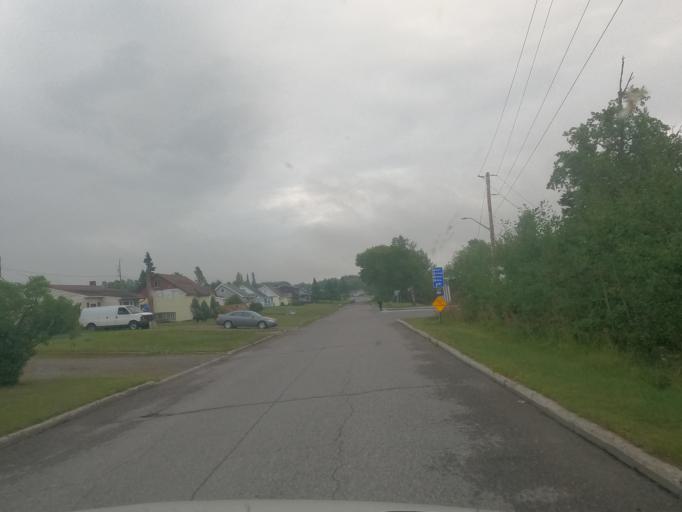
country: CA
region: Ontario
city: Marathon
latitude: 48.7807
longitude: -87.1031
